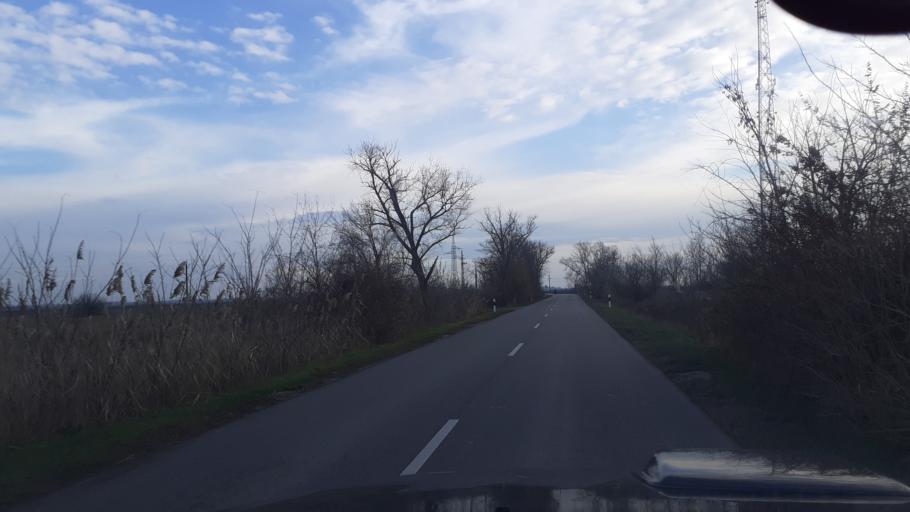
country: HU
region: Bacs-Kiskun
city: Szabadszallas
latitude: 46.9254
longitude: 19.1770
